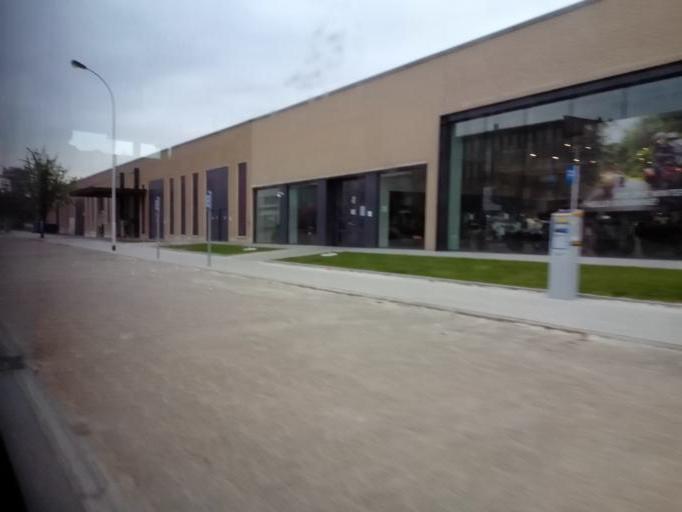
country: BE
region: Flanders
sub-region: Provincie Vlaams-Brabant
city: Diegem
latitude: 50.8569
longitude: 4.4125
